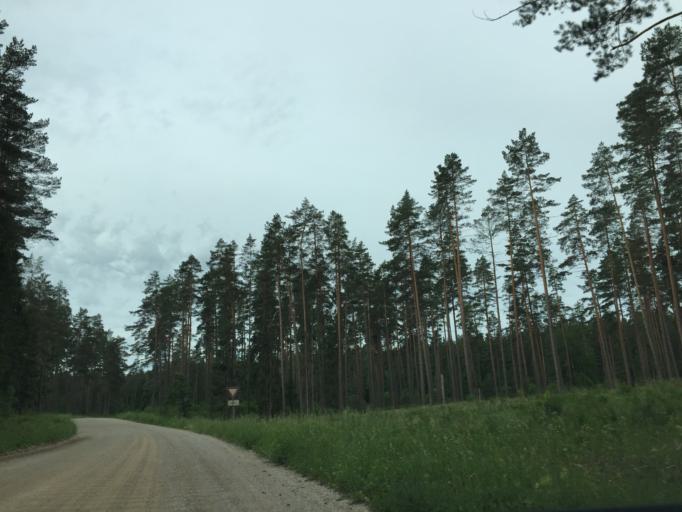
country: LV
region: Tukuma Rajons
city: Tukums
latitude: 57.0000
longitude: 23.1496
